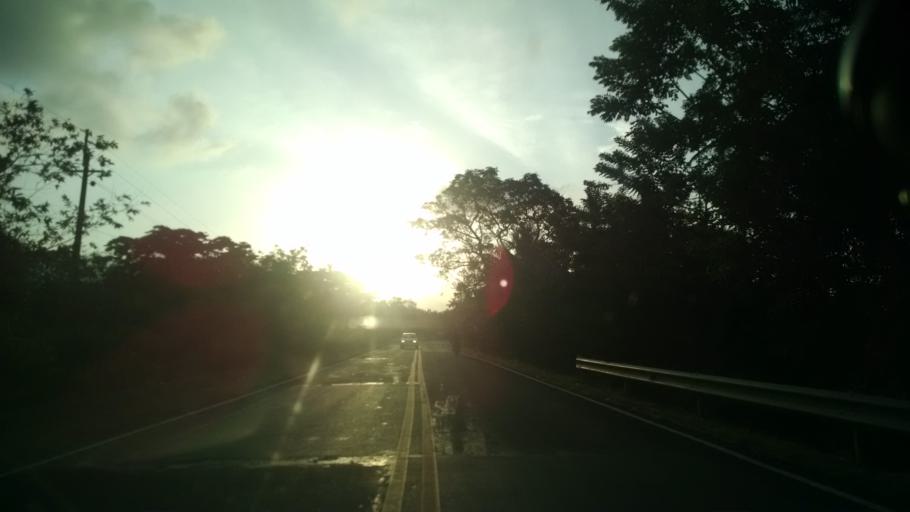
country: CO
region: Antioquia
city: San Juan de Uraba
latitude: 8.7363
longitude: -76.5624
